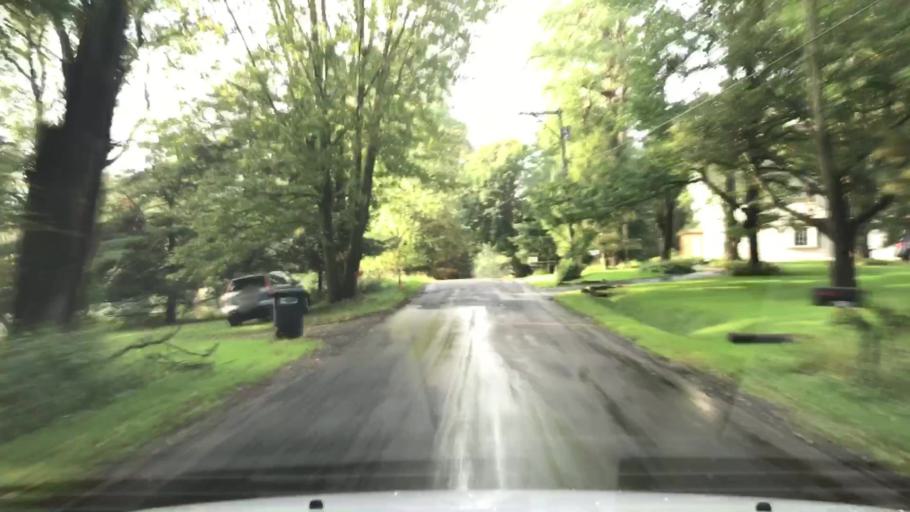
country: US
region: New York
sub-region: Cattaraugus County
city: Little Valley
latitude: 42.3109
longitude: -78.7187
